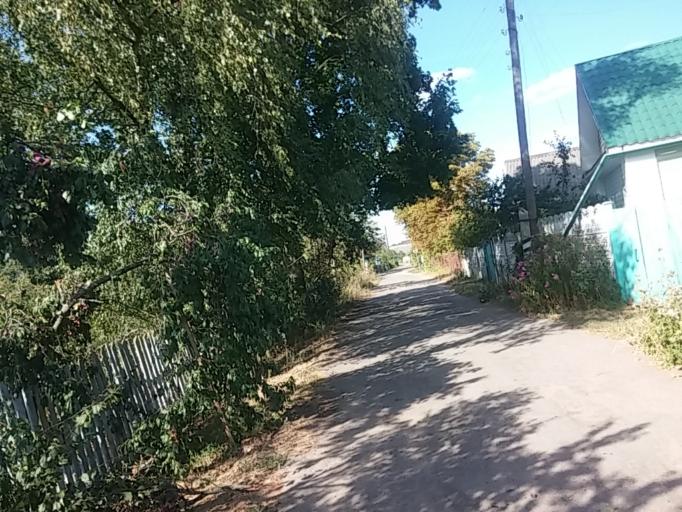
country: BY
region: Minsk
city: Chervyen'
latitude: 53.7763
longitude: 28.2664
